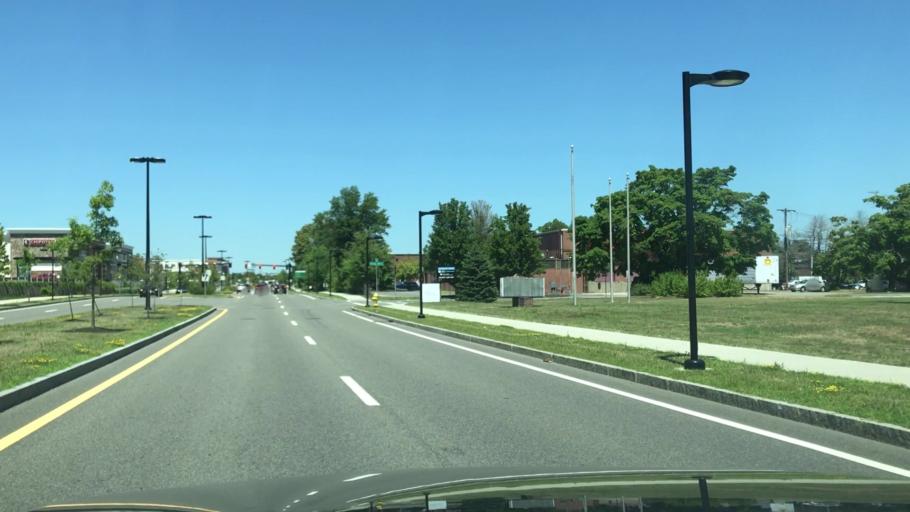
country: US
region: Massachusetts
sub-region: Norfolk County
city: Dedham
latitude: 42.2032
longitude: -71.1537
